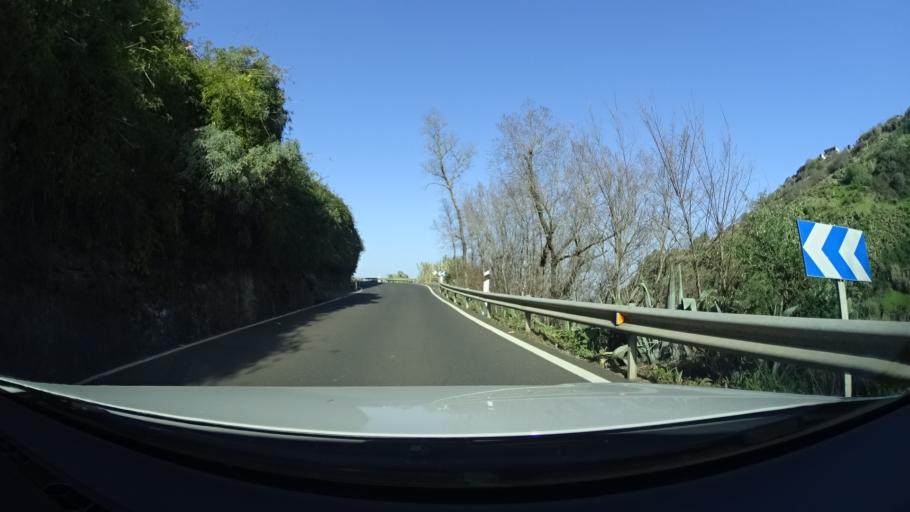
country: ES
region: Canary Islands
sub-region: Provincia de Las Palmas
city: Valleseco
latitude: 28.0257
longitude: -15.5566
